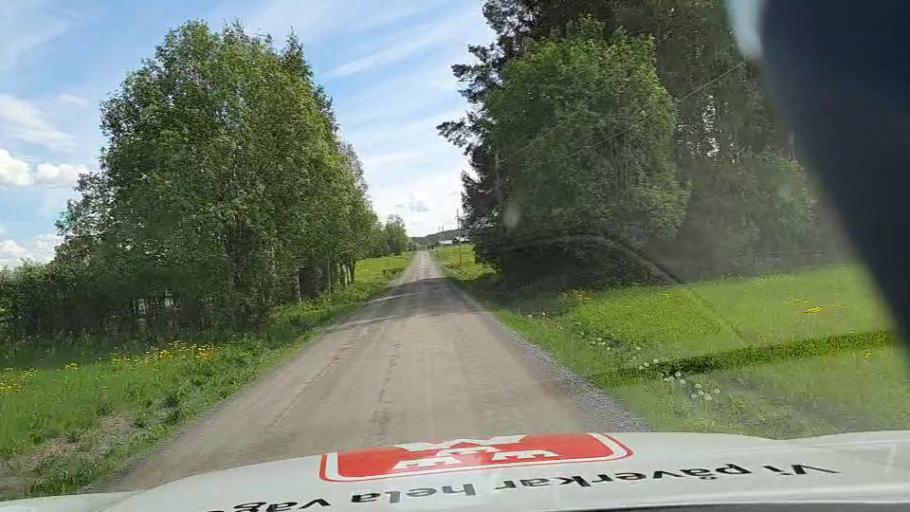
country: SE
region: Jaemtland
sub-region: OEstersunds Kommun
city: Brunflo
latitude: 62.9904
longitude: 14.8086
